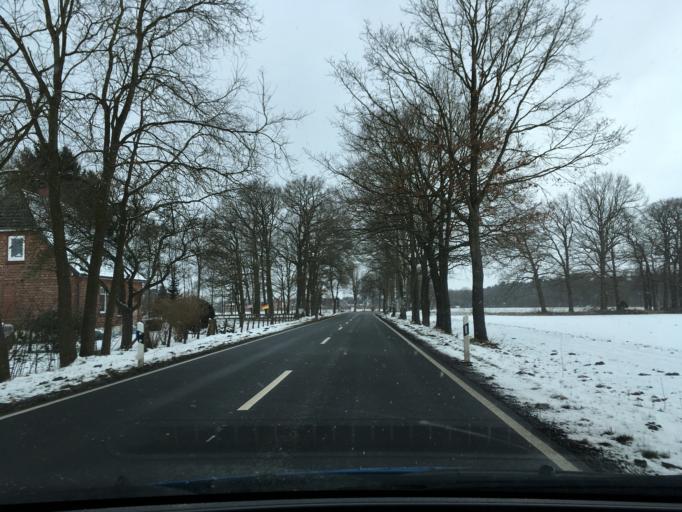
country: DE
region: Lower Saxony
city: Garstedt
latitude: 53.2968
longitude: 10.1907
